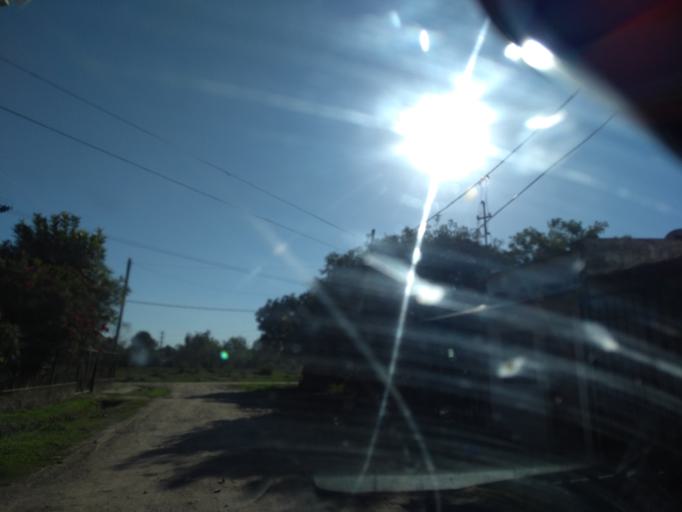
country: AR
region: Chaco
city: Resistencia
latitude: -27.4739
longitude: -58.9705
